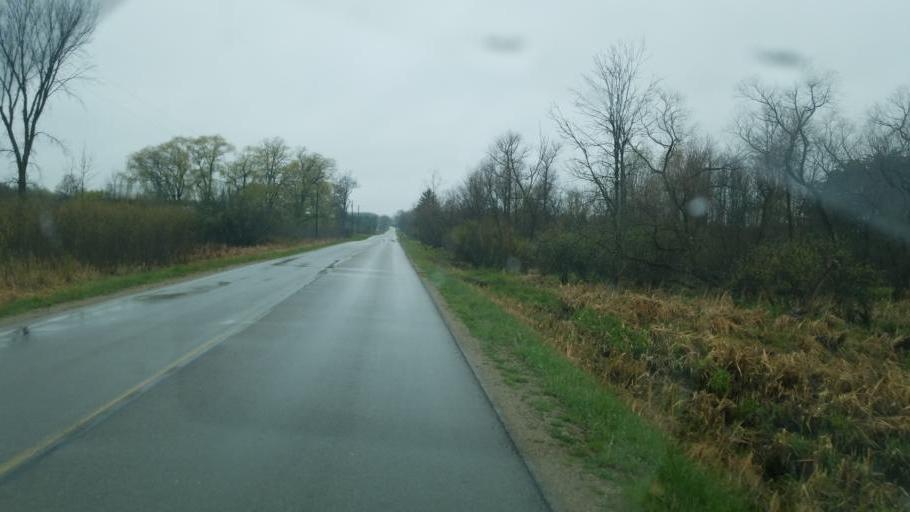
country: US
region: Michigan
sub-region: Montcalm County
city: Lakeview
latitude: 43.4895
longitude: -85.3252
